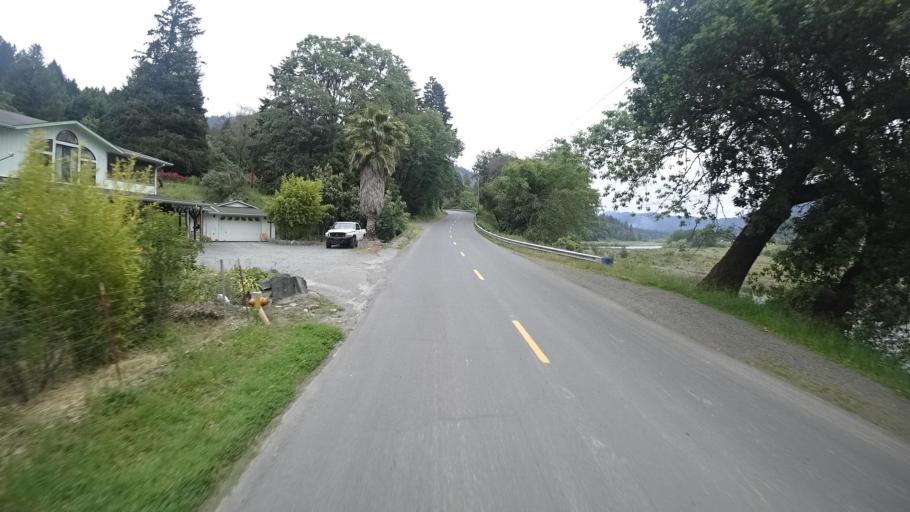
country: US
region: California
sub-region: Humboldt County
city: Willow Creek
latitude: 41.0601
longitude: -123.6798
